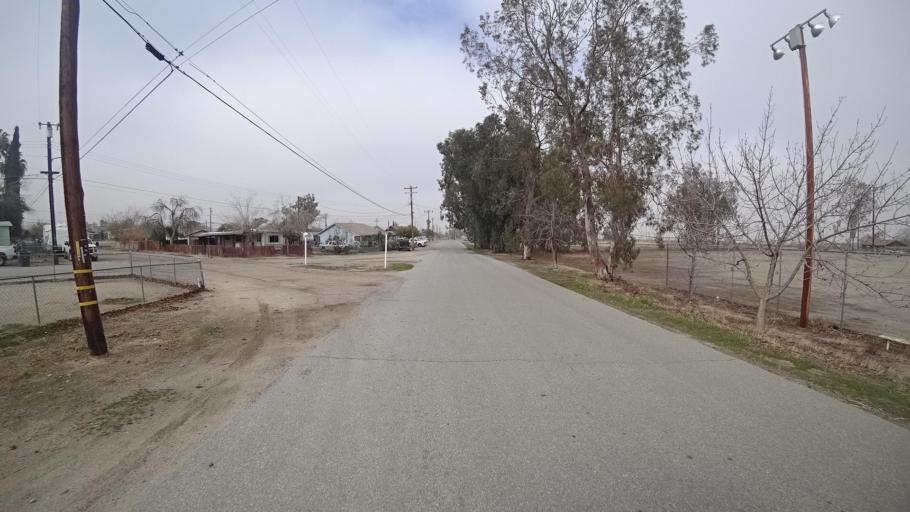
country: US
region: California
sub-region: Kern County
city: Maricopa
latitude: 35.0570
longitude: -119.3965
